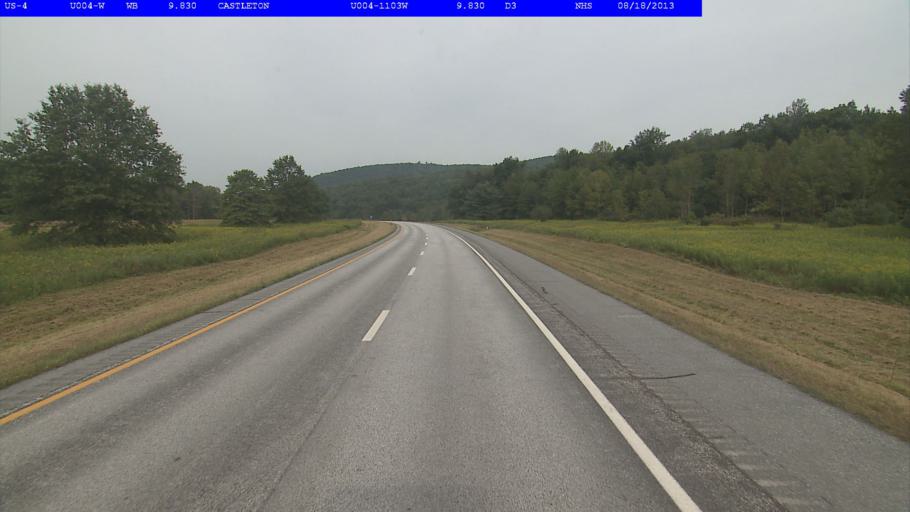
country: US
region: Vermont
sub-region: Rutland County
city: Castleton
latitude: 43.6170
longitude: -73.1238
